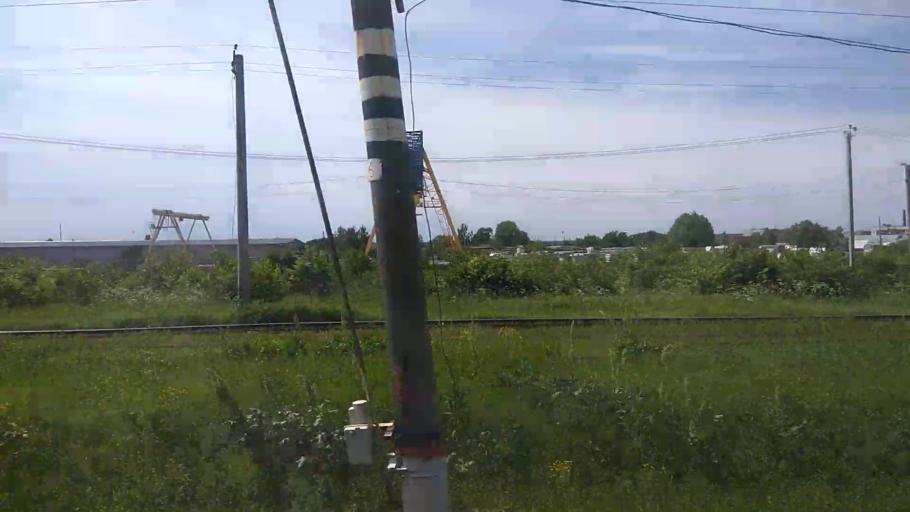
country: RU
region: Moskovskaya
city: Malyshevo
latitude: 55.5069
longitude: 38.3494
